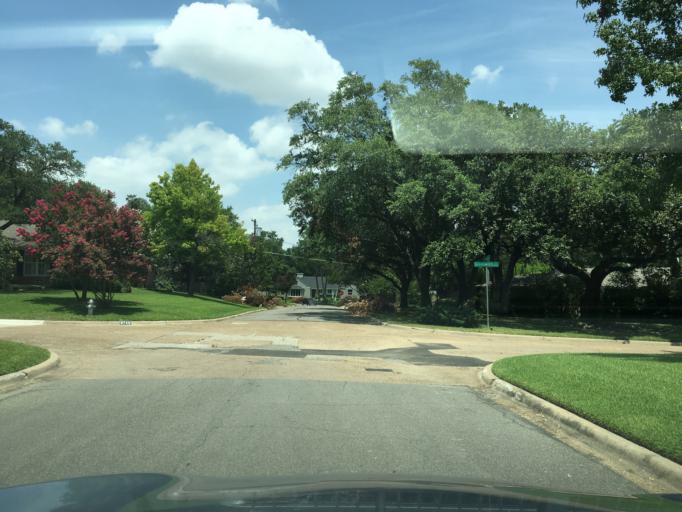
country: US
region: Texas
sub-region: Dallas County
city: University Park
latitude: 32.9113
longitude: -96.7883
